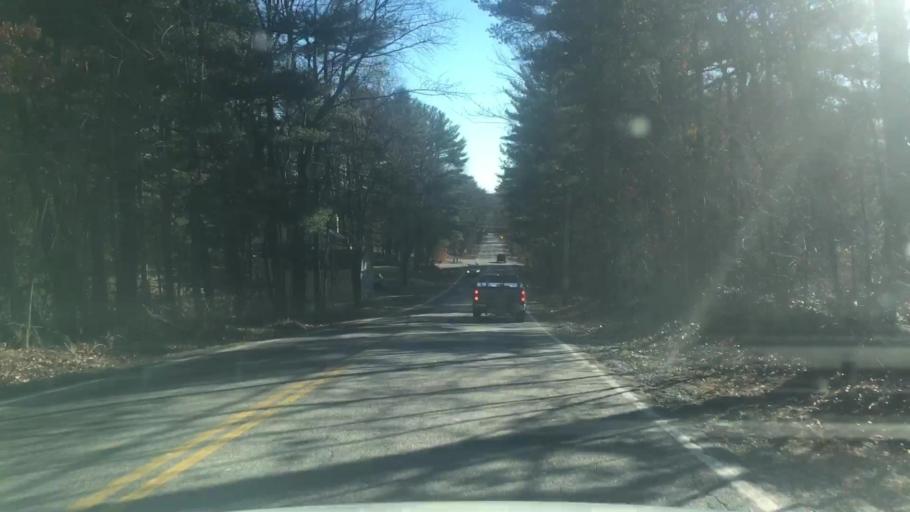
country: US
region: New Hampshire
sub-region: Rockingham County
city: Londonderry
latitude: 42.8996
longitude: -71.4143
